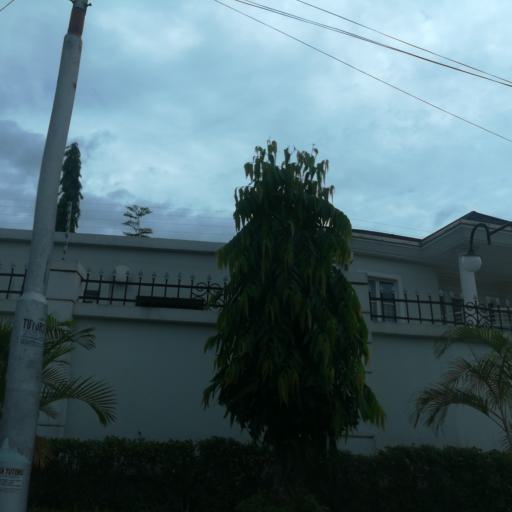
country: NG
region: Lagos
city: Ikoyi
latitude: 6.4463
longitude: 3.4666
